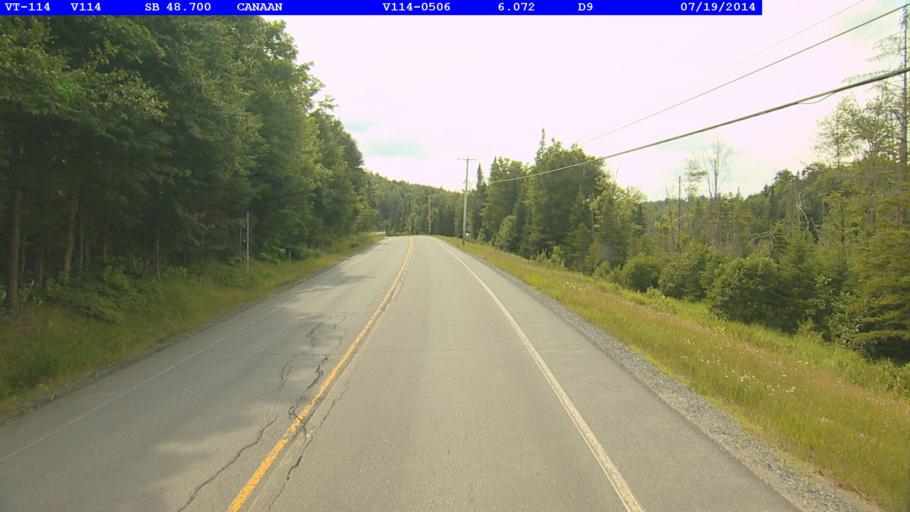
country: US
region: New Hampshire
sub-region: Coos County
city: Colebrook
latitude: 45.0091
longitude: -71.5743
